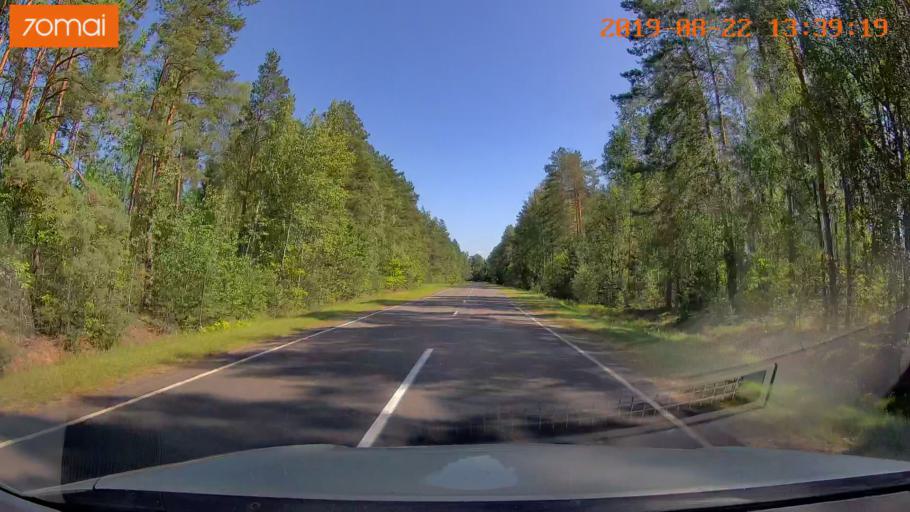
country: BY
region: Minsk
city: Staryya Darohi
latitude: 53.2278
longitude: 28.3464
